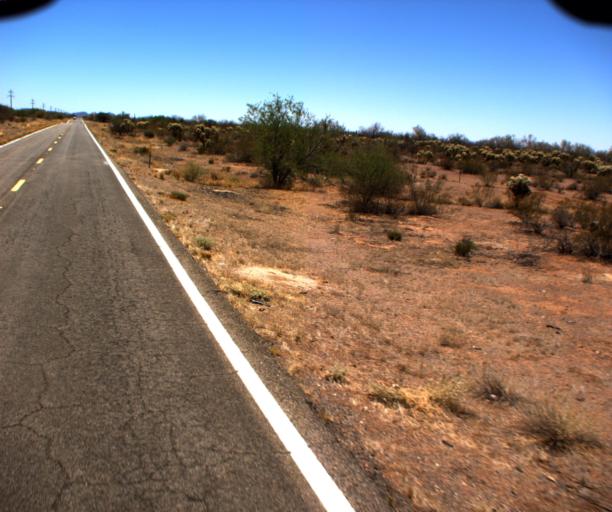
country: US
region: Arizona
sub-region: Pima County
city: Sells
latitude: 32.0821
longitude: -112.0511
